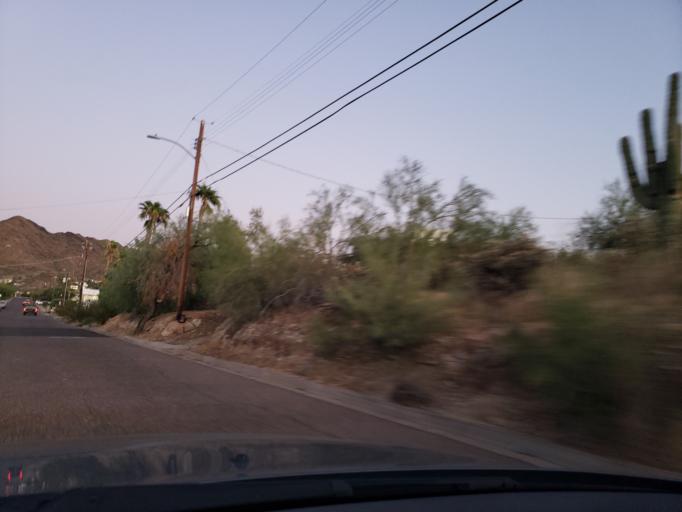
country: US
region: Arizona
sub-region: Maricopa County
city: Paradise Valley
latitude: 33.5767
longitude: -112.0514
